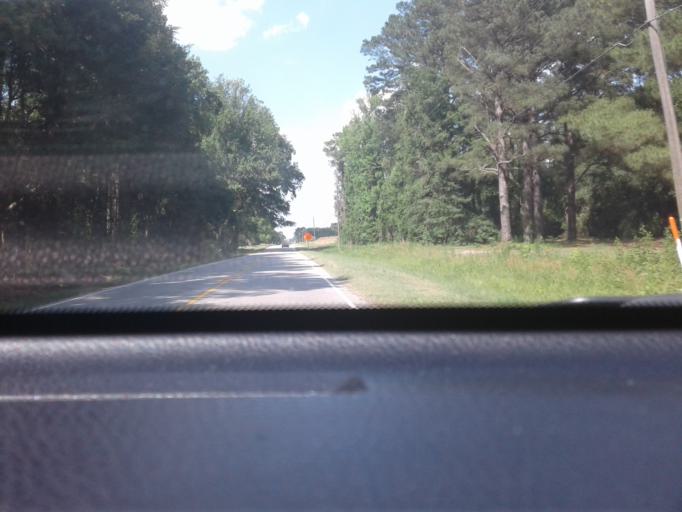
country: US
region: North Carolina
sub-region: Harnett County
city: Erwin
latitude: 35.1922
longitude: -78.6963
